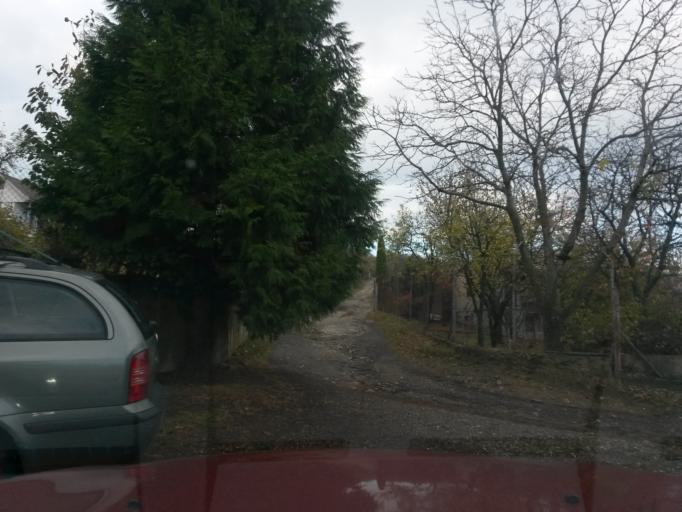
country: SK
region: Kosicky
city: Kosice
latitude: 48.7661
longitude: 21.2185
